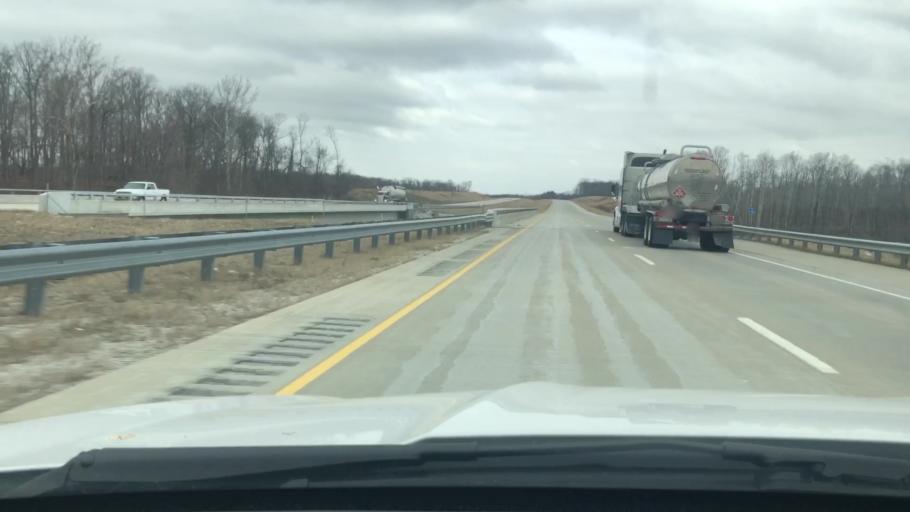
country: US
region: Indiana
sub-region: Carroll County
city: Delphi
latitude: 40.5795
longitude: -86.6483
